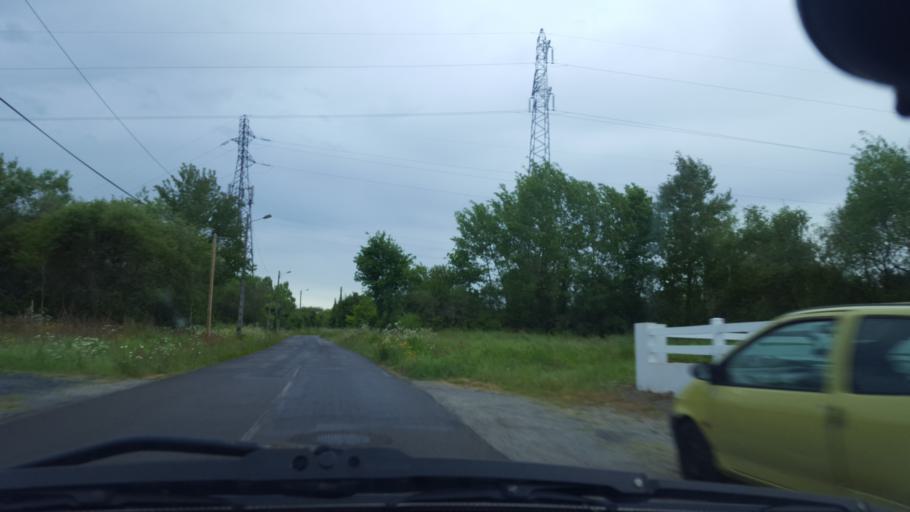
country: FR
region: Pays de la Loire
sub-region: Departement de la Loire-Atlantique
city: Les Sorinieres
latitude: 47.1686
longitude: -1.5272
